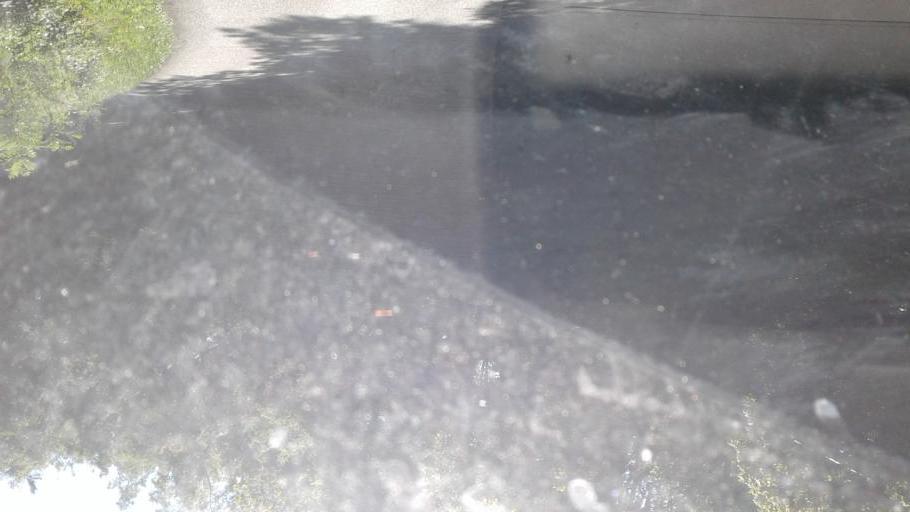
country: FR
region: Rhone-Alpes
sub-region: Departement de l'Ain
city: Artemare
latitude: 45.8748
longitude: 5.6763
